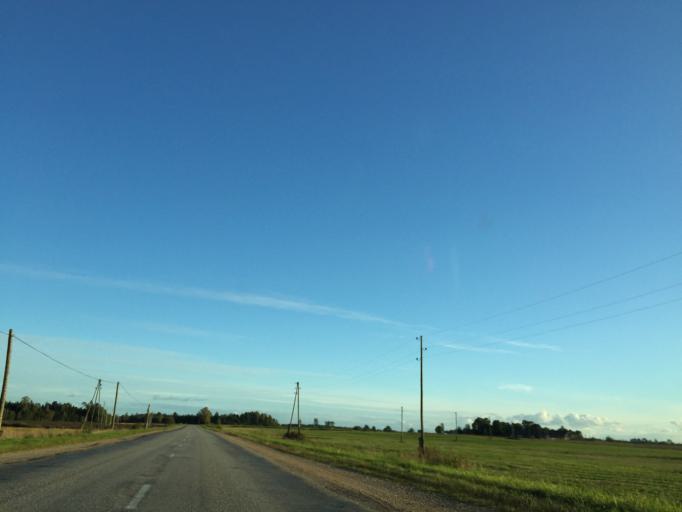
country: LV
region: Saldus Rajons
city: Saldus
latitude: 56.7398
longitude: 22.3774
